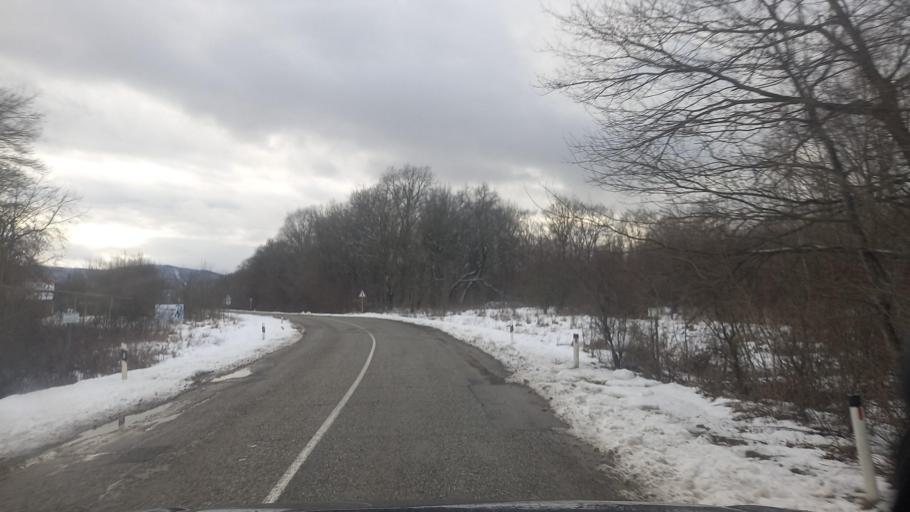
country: RU
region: Krasnodarskiy
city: Smolenskaya
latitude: 44.7277
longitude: 38.8345
